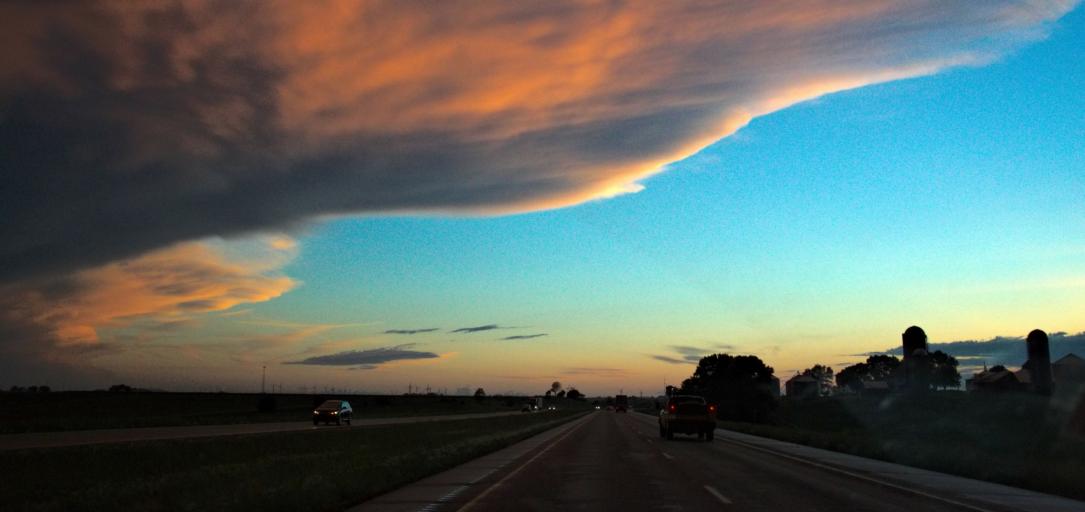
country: US
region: Iowa
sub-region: Cass County
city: Atlantic
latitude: 41.4976
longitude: -95.0846
